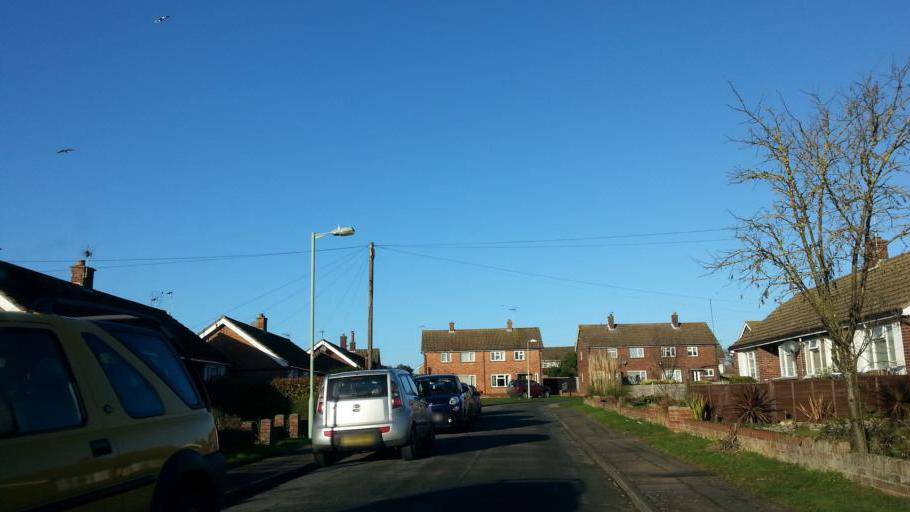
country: GB
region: England
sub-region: Suffolk
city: Felixstowe
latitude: 51.9791
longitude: 1.3160
